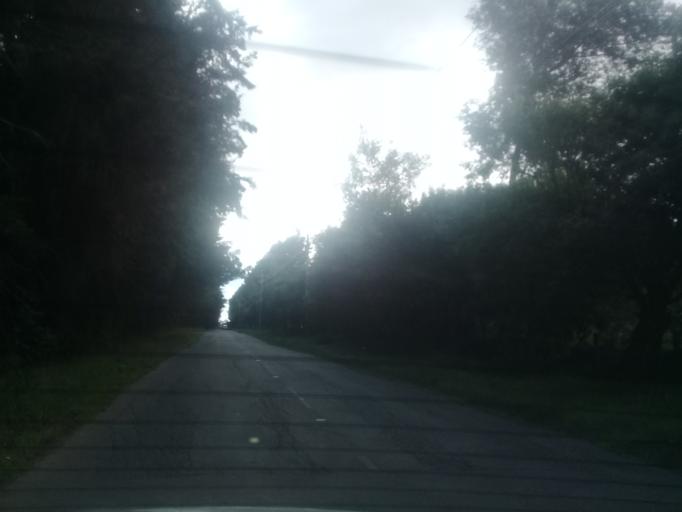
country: CO
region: Cundinamarca
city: Subachoque
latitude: 4.9108
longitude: -74.1863
